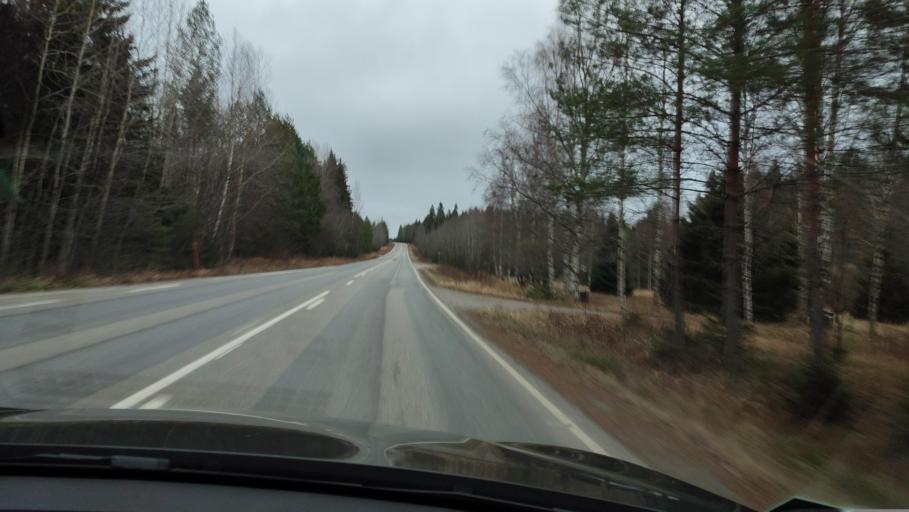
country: FI
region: Southern Ostrobothnia
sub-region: Suupohja
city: Karijoki
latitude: 62.2371
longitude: 21.6936
